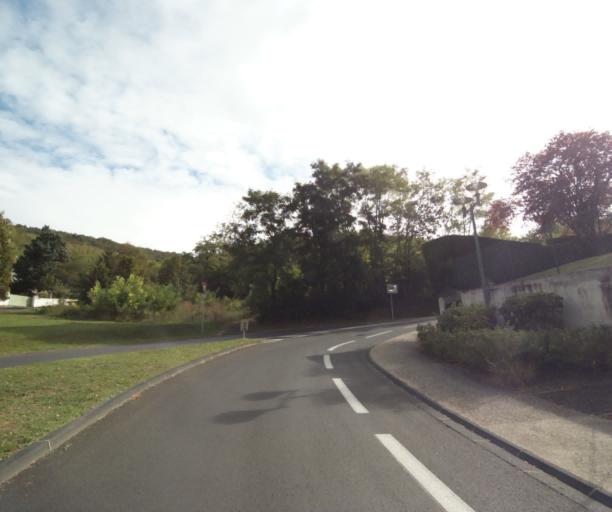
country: FR
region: Auvergne
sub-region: Departement du Puy-de-Dome
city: Romagnat
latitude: 45.7254
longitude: 3.1012
